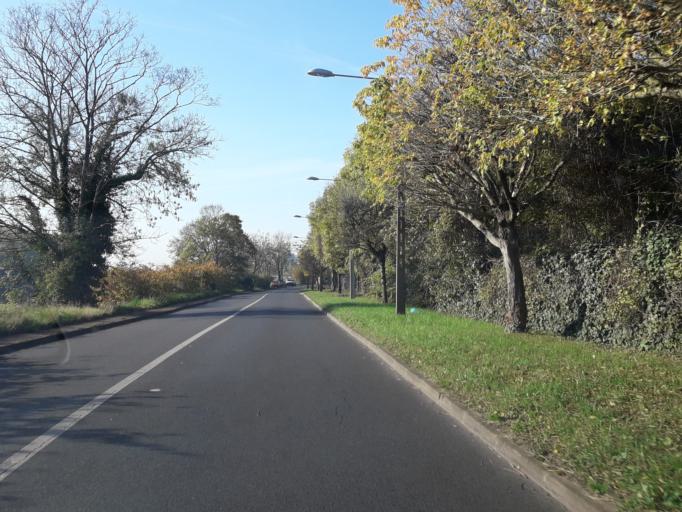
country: FR
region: Ile-de-France
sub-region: Departement de l'Essonne
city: Vigneux-sur-Seine
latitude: 48.7165
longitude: 2.4100
